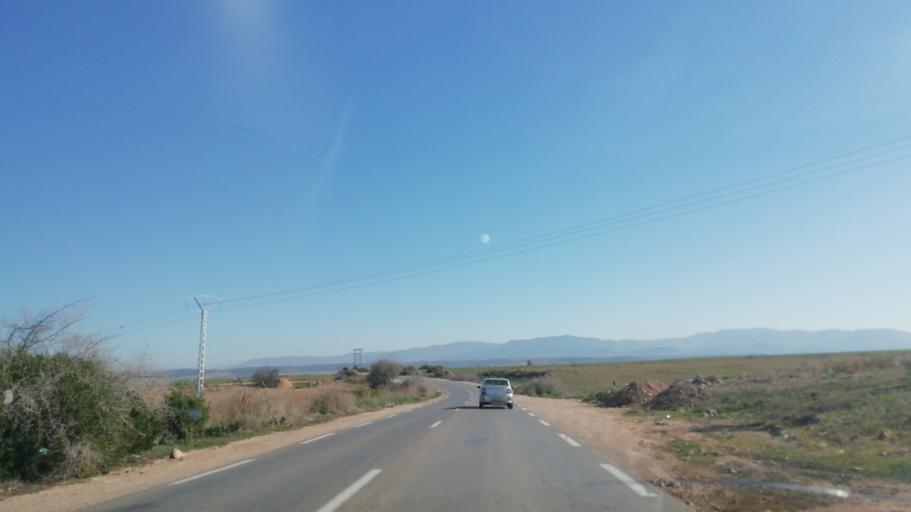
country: DZ
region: Tlemcen
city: Nedroma
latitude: 34.8331
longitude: -1.6803
